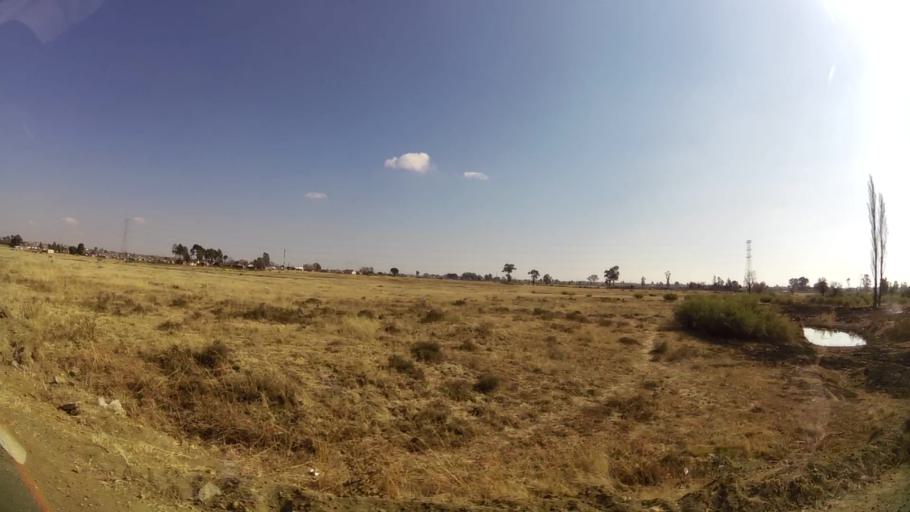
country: ZA
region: Orange Free State
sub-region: Mangaung Metropolitan Municipality
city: Bloemfontein
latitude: -29.1735
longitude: 26.3073
